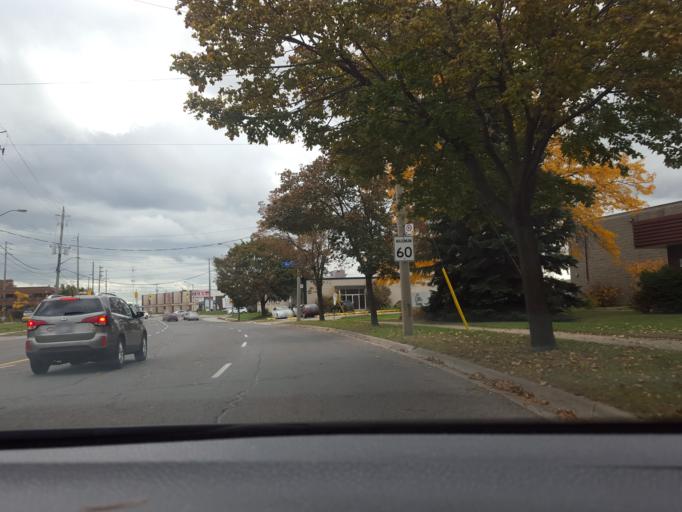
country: CA
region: Ontario
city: Etobicoke
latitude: 43.6218
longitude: -79.5500
